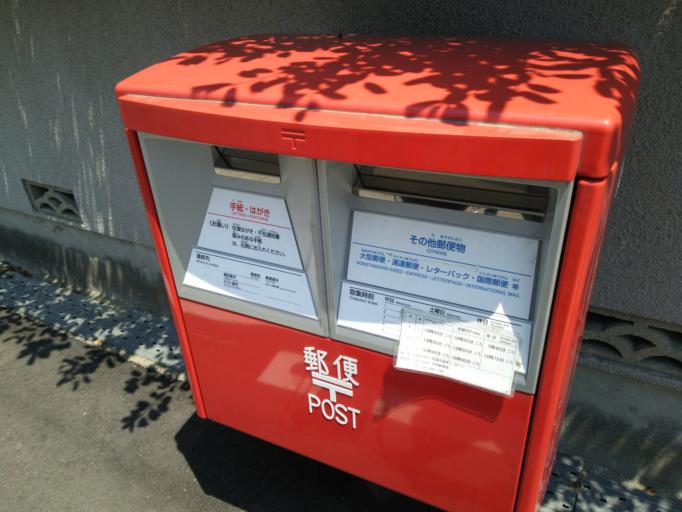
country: JP
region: Hyogo
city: Amagasaki
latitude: 34.7217
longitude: 135.4416
